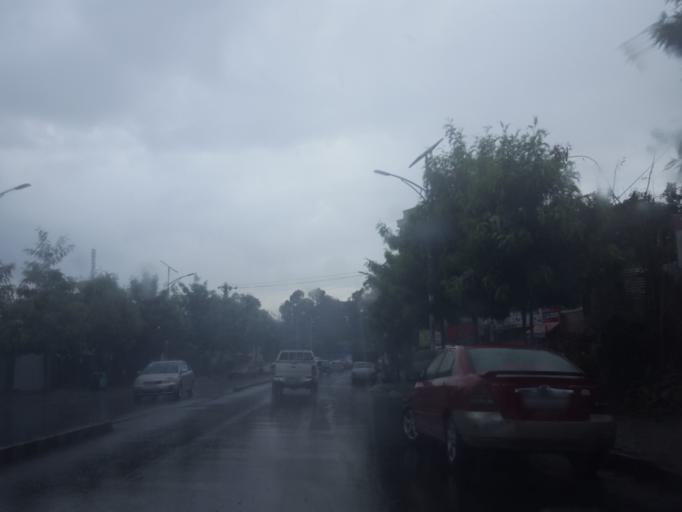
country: ET
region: Adis Abeba
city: Addis Ababa
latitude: 9.0220
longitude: 38.7817
